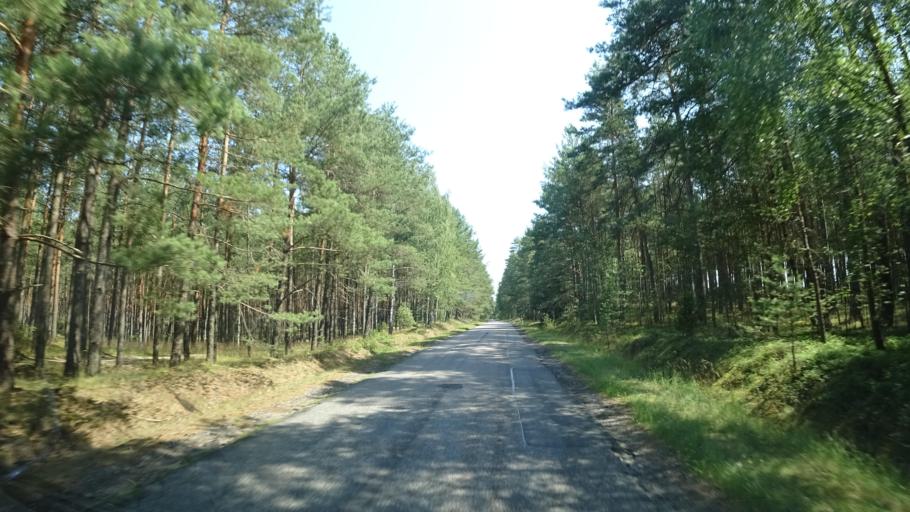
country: PL
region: Pomeranian Voivodeship
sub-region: Powiat chojnicki
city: Brusy
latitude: 53.8554
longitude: 17.5832
